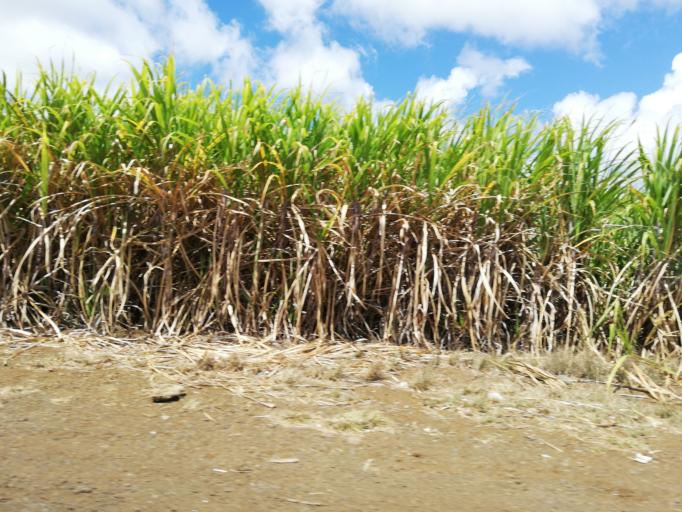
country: MU
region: Riviere du Rempart
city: Cottage
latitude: -20.0695
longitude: 57.6242
